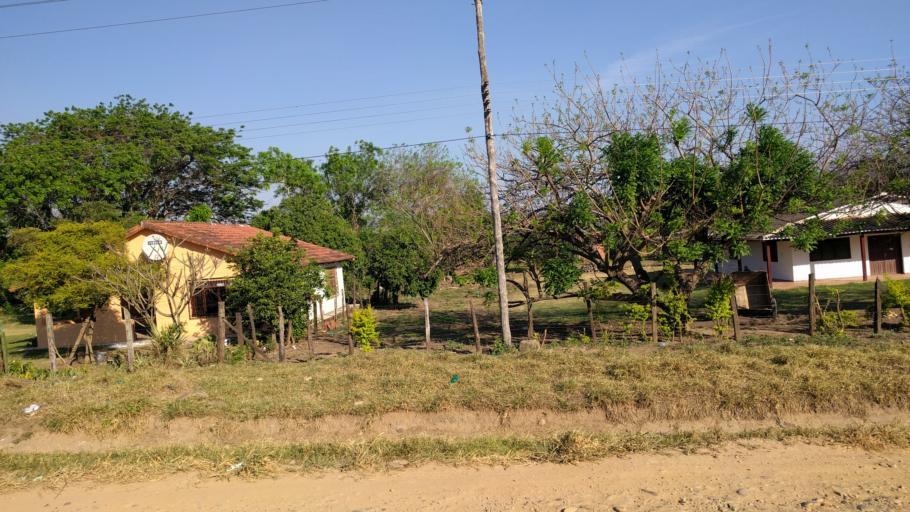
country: BO
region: Santa Cruz
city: Jorochito
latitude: -18.1458
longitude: -63.4835
